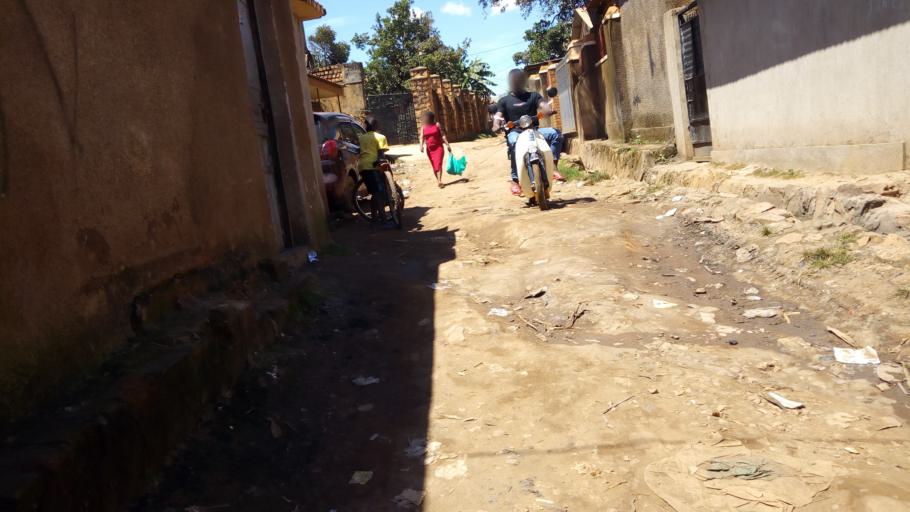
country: UG
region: Central Region
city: Kampala Central Division
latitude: 0.3554
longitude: 32.5592
